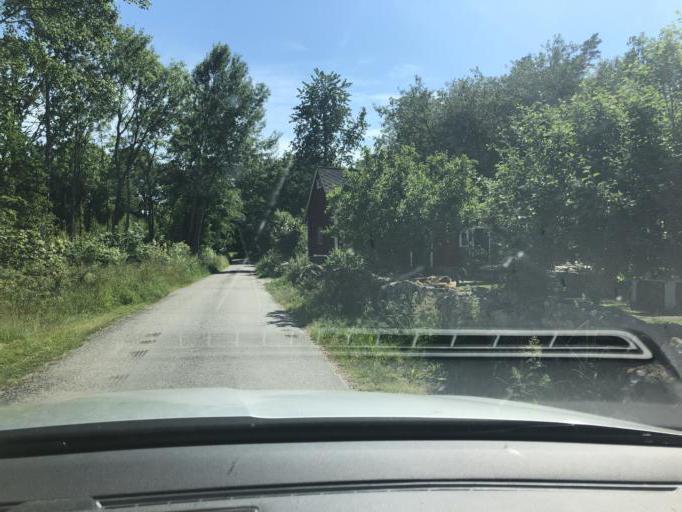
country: SE
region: Blekinge
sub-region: Karlshamns Kommun
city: Morrum
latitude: 56.1849
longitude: 14.7008
